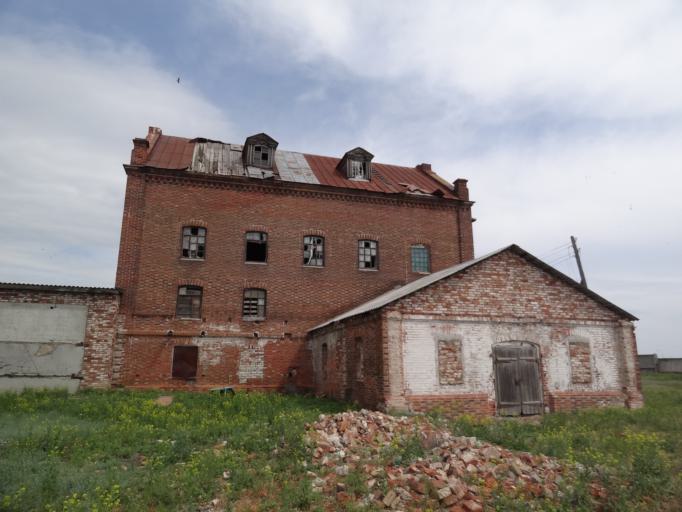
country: RU
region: Saratov
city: Privolzhskiy
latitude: 51.1987
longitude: 45.9080
